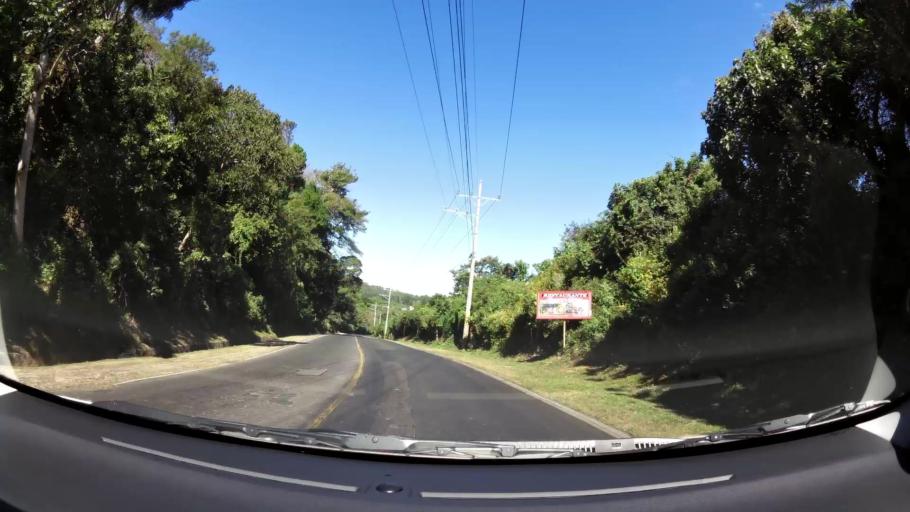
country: SV
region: Ahuachapan
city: Concepcion de Ataco
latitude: 13.8626
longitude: -89.8484
